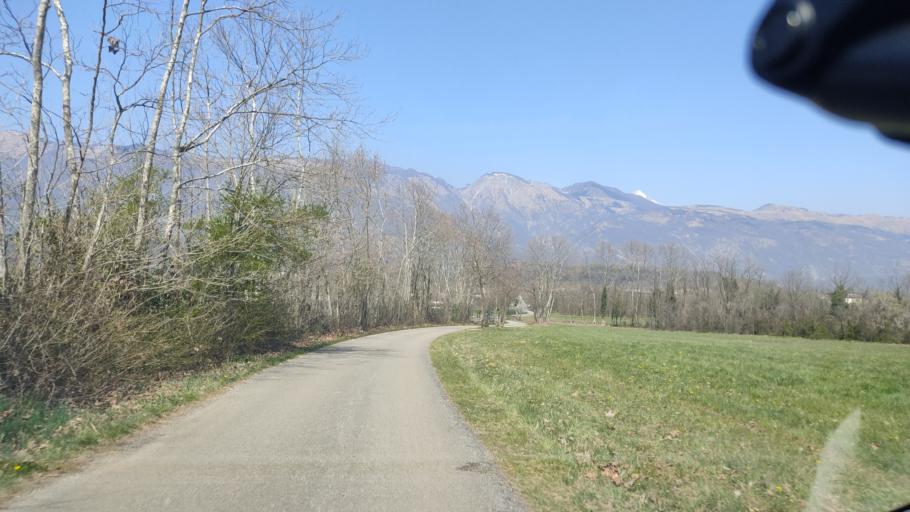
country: IT
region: Friuli Venezia Giulia
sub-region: Provincia di Pordenone
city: Budoia
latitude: 46.0269
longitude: 12.5353
